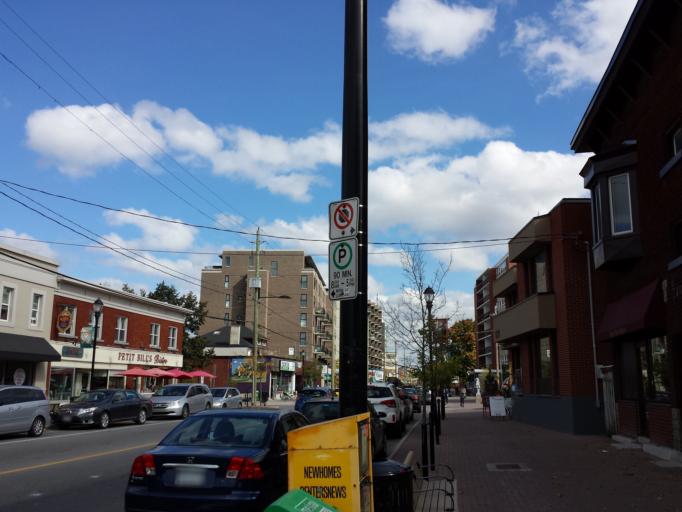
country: CA
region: Ontario
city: Ottawa
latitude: 45.3988
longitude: -75.7359
